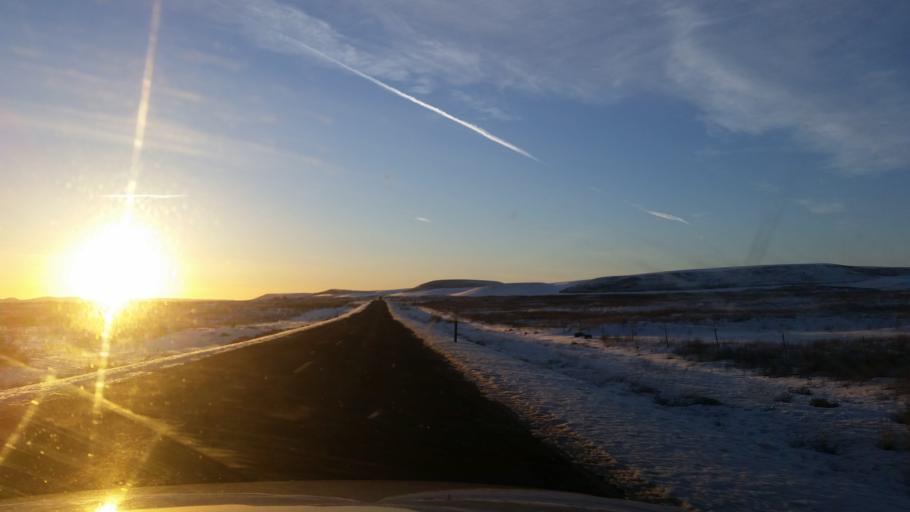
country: US
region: Washington
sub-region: Spokane County
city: Cheney
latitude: 47.1159
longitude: -117.7935
